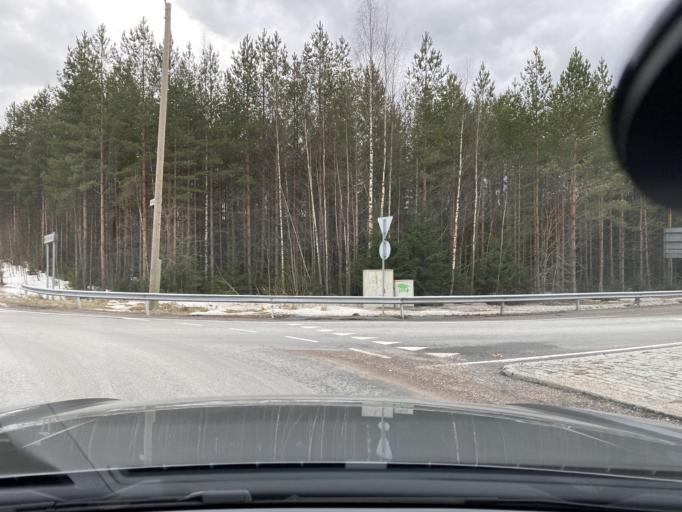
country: FI
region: Uusimaa
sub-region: Helsinki
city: Hyvinge
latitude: 60.6609
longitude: 24.7979
